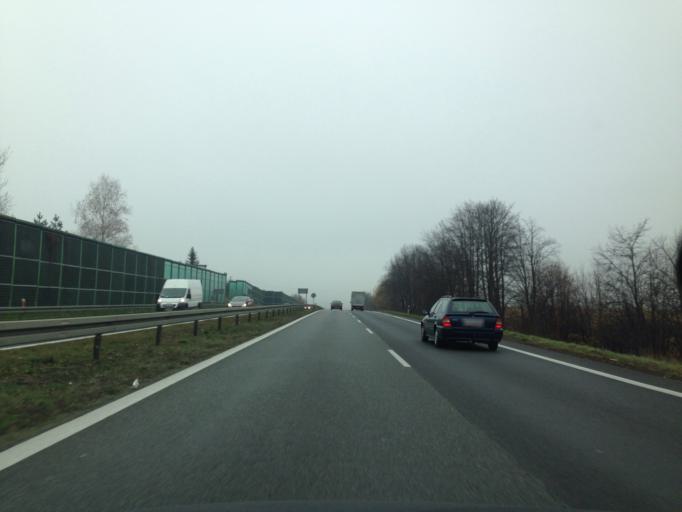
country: PL
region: Silesian Voivodeship
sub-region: Powiat bedzinski
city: Sarnow
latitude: 50.3731
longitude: 19.1448
